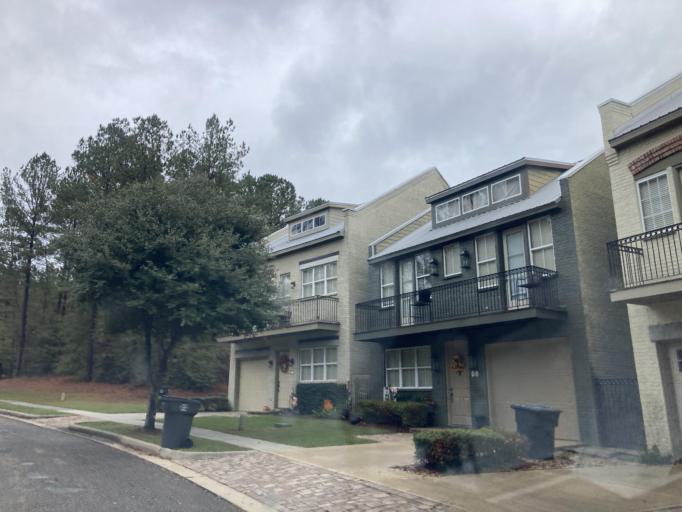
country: US
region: Mississippi
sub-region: Lamar County
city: West Hattiesburg
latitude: 31.2850
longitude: -89.4760
